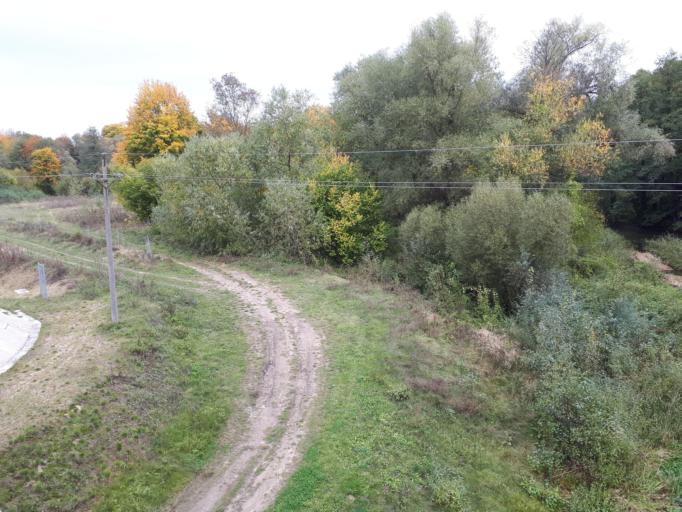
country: LT
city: Kalvarija
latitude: 54.4236
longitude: 23.3122
